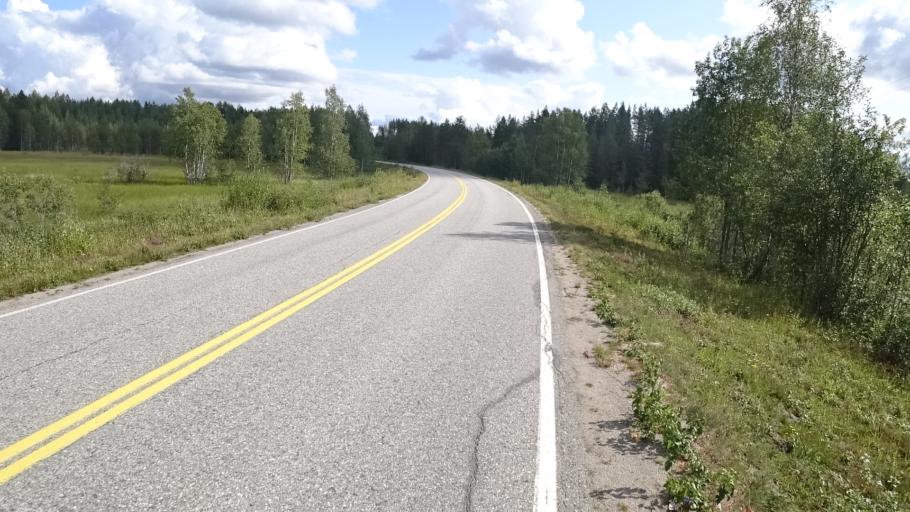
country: FI
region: North Karelia
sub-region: Joensuu
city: Ilomantsi
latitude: 62.6176
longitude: 31.2053
